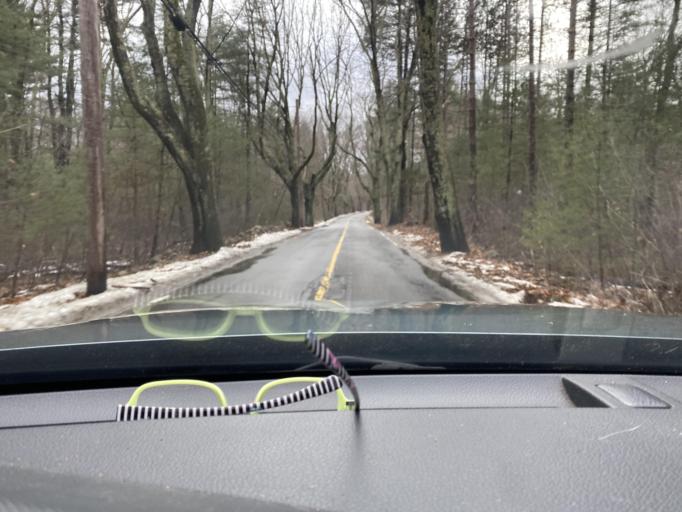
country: US
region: Massachusetts
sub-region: Middlesex County
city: Sherborn
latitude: 42.2267
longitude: -71.3673
